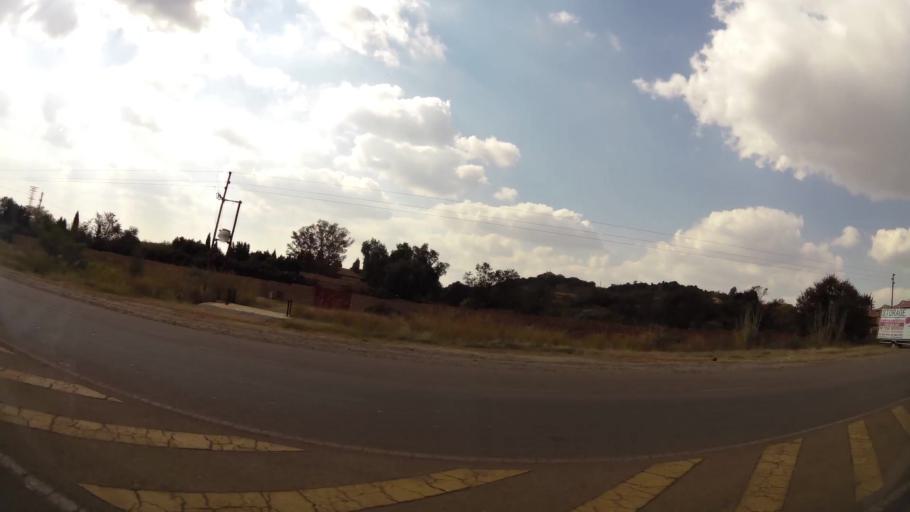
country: ZA
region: Gauteng
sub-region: City of Tshwane Metropolitan Municipality
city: Centurion
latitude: -25.8109
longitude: 28.3320
